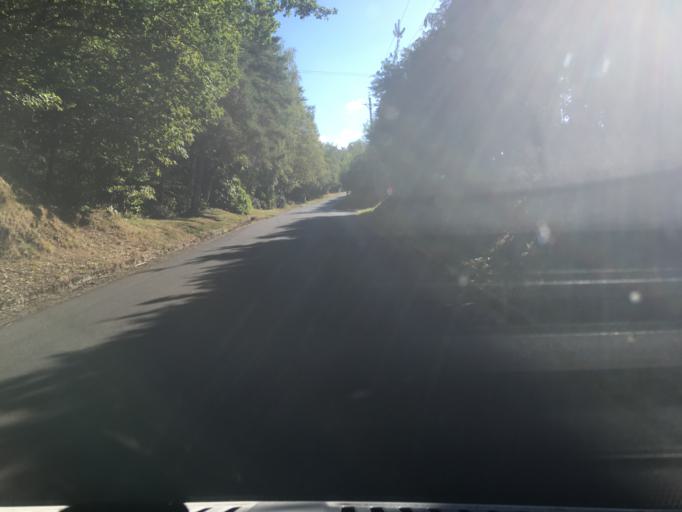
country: FR
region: Auvergne
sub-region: Departement du Cantal
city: Lanobre
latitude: 45.4429
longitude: 2.5141
